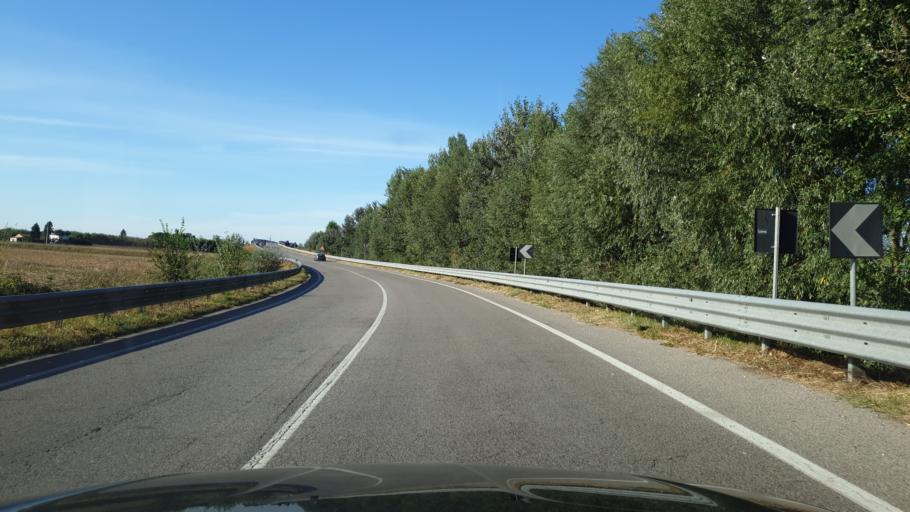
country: IT
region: Emilia-Romagna
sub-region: Provincia di Ravenna
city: Alfonsine
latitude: 44.5025
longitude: 12.0618
